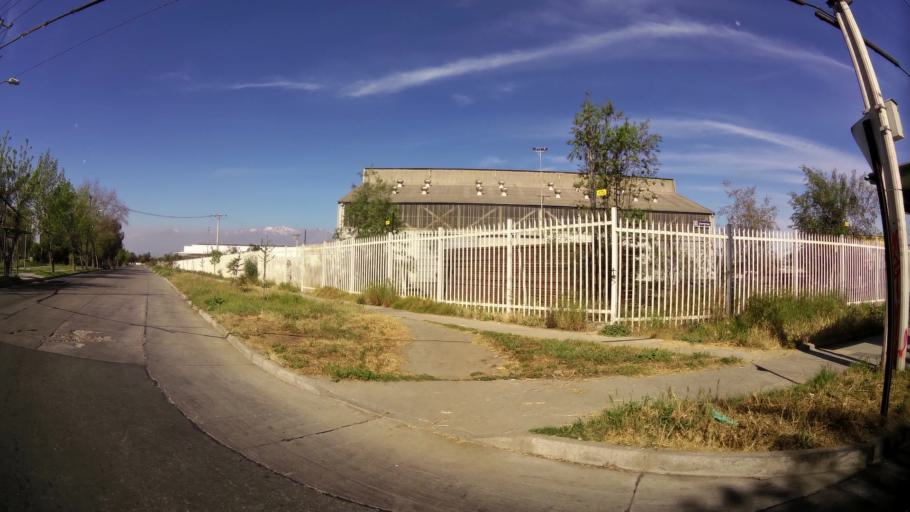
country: CL
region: Santiago Metropolitan
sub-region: Provincia de Santiago
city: Lo Prado
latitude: -33.4879
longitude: -70.7164
